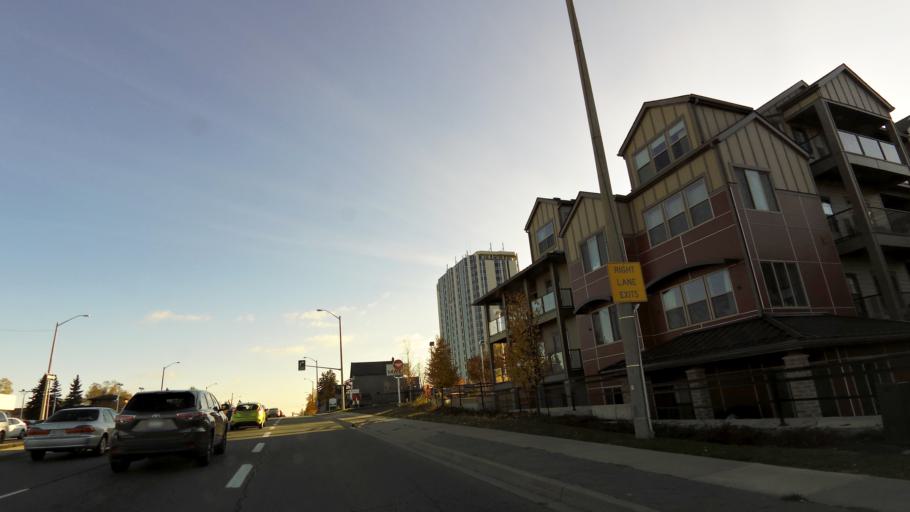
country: CA
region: Ontario
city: Cambridge
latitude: 43.3849
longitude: -80.3209
